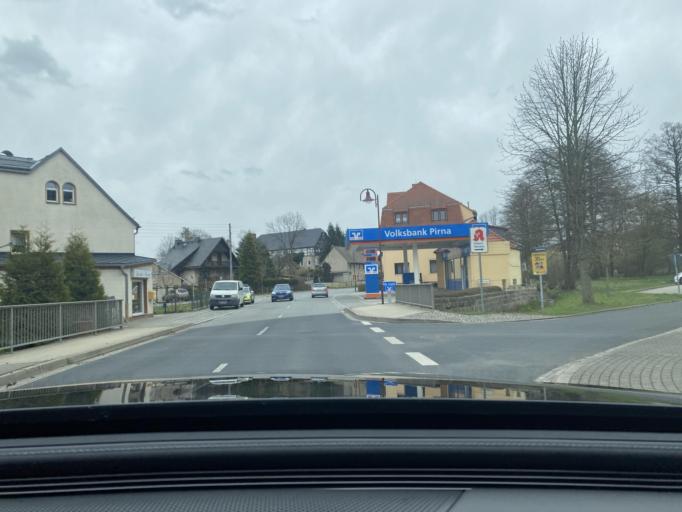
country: DE
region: Saxony
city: Durrrohrsdorf
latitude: 51.0352
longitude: 13.9936
